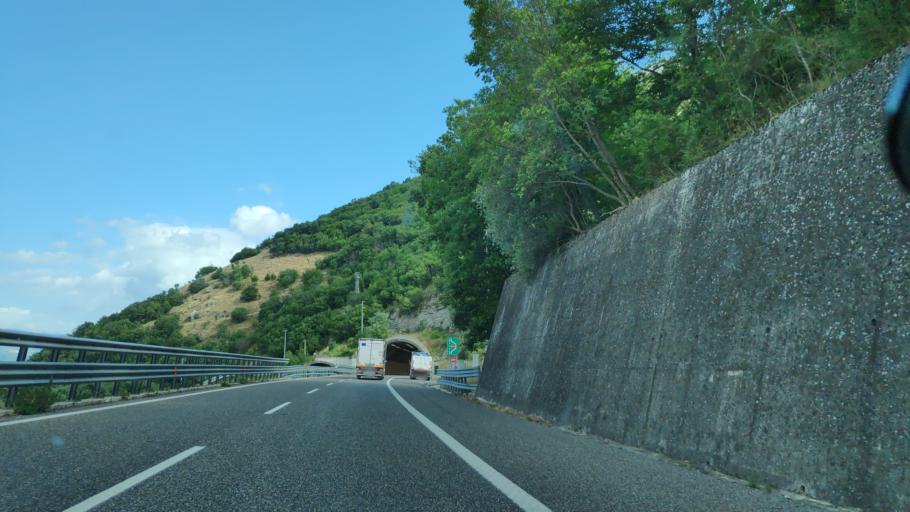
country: IT
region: Campania
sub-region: Provincia di Salerno
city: Sicignano degli Alburni
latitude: 40.5843
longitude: 15.3406
